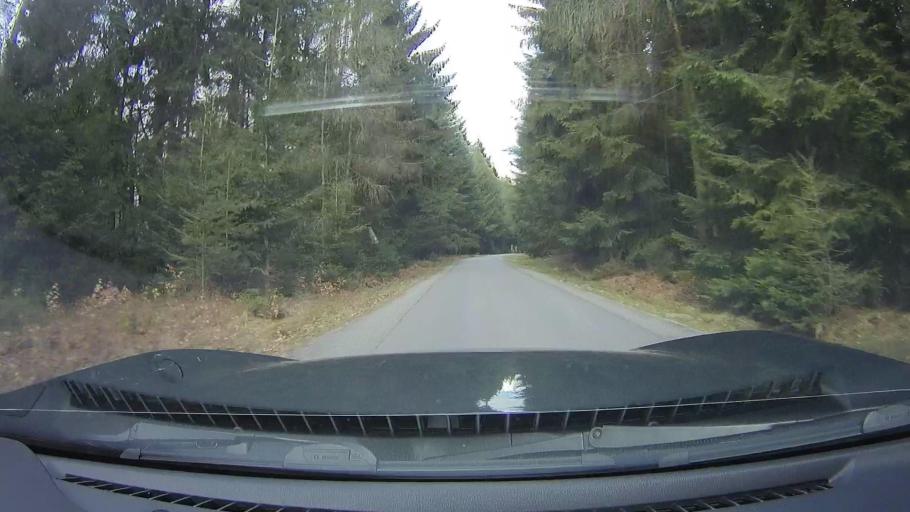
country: DE
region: Hesse
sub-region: Regierungsbezirk Darmstadt
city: Hesseneck
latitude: 49.6069
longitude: 9.0790
